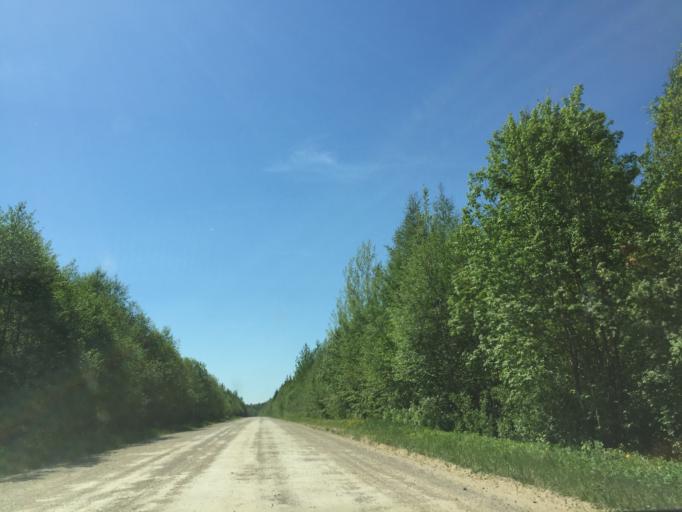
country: LV
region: Kegums
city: Kegums
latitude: 56.8762
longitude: 24.7788
